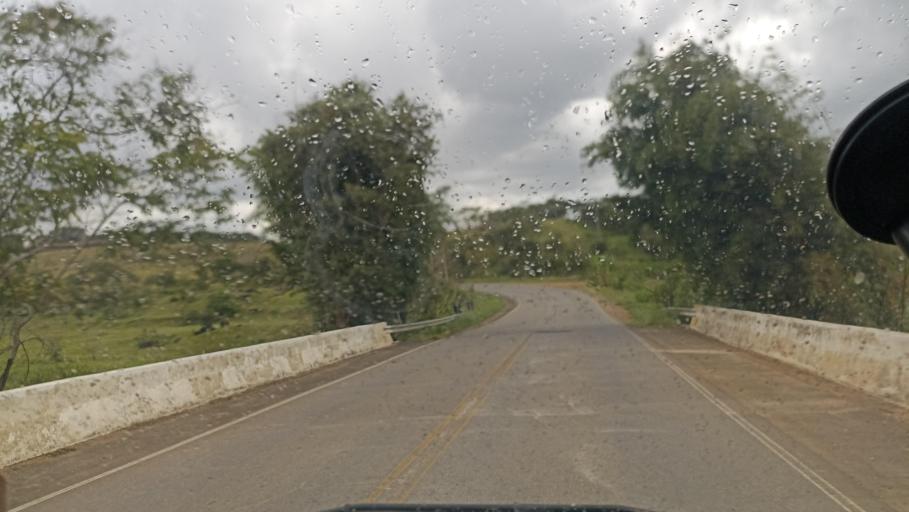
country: BR
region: Minas Gerais
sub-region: Baependi
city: Baependi
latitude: -21.9200
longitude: -44.8251
